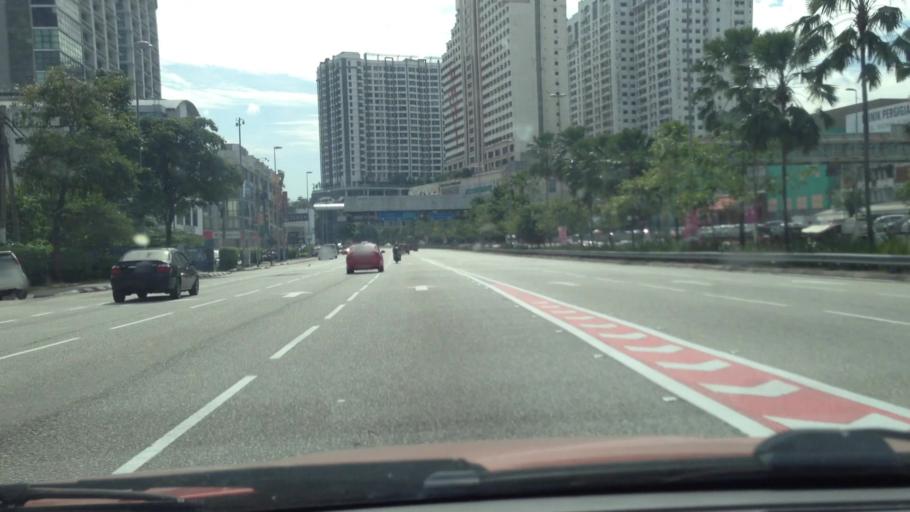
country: MY
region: Kuala Lumpur
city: Kuala Lumpur
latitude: 3.0834
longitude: 101.6703
